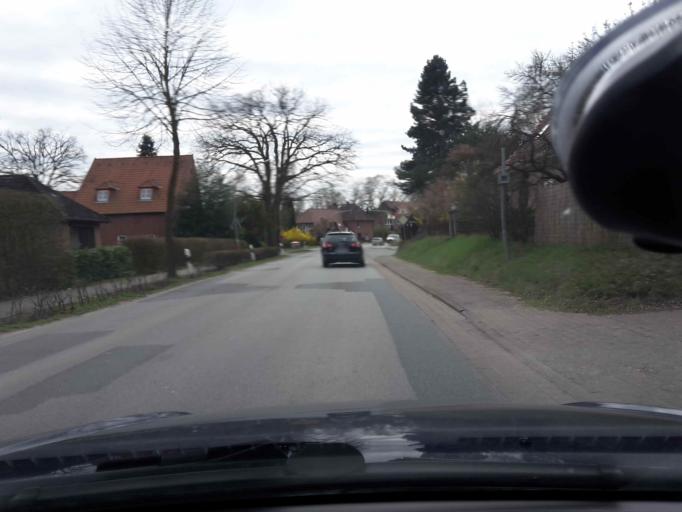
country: DE
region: Lower Saxony
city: Harmstorf
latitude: 53.3510
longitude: 9.9910
